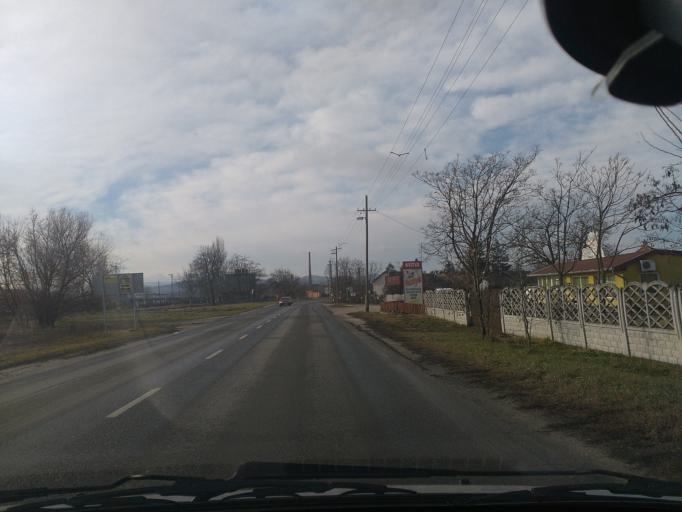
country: HU
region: Komarom-Esztergom
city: Tokod
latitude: 47.7356
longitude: 18.6775
